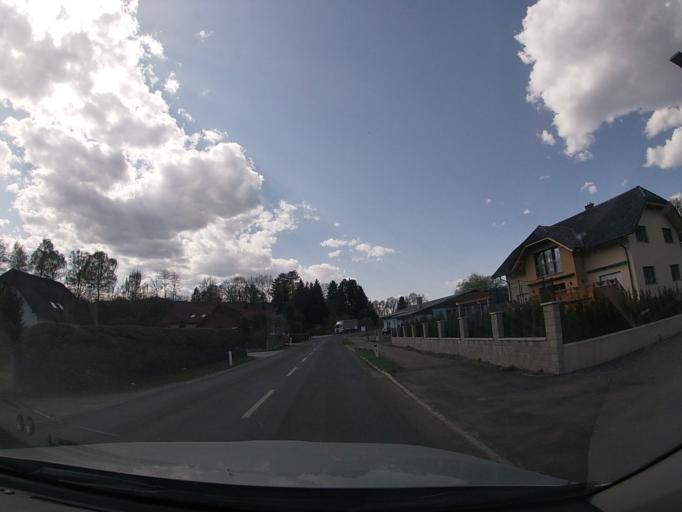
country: AT
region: Styria
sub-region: Politischer Bezirk Murtal
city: Fohnsdorf
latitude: 47.1935
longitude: 14.6671
